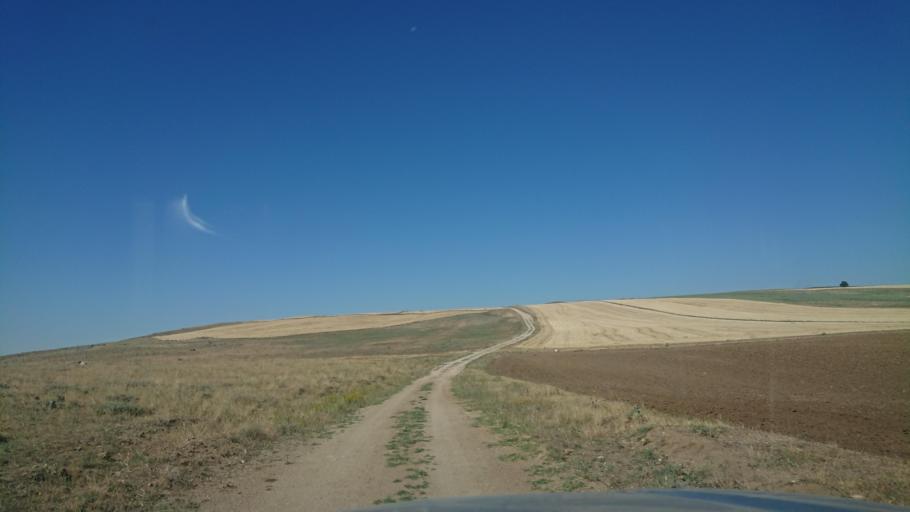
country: TR
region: Aksaray
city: Sariyahsi
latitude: 38.9269
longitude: 33.8529
